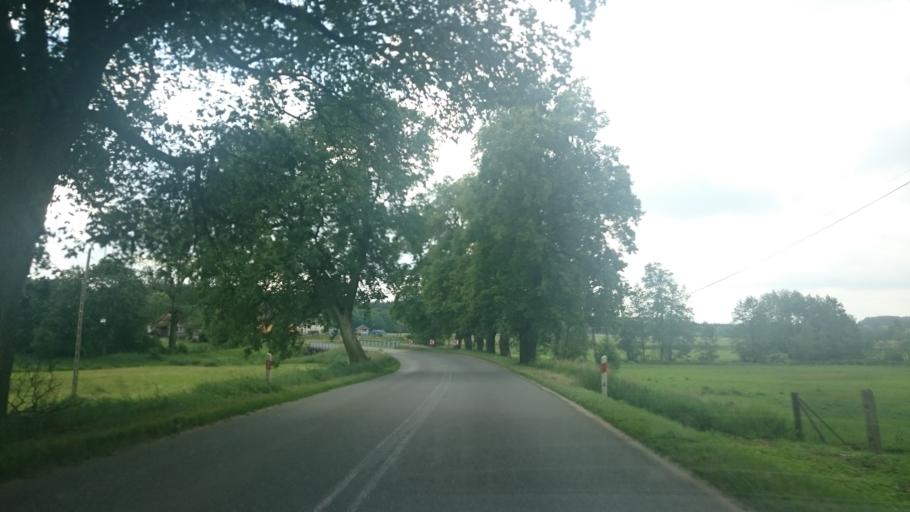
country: PL
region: Pomeranian Voivodeship
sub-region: Powiat koscierski
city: Stara Kiszewa
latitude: 53.9768
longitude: 18.2288
